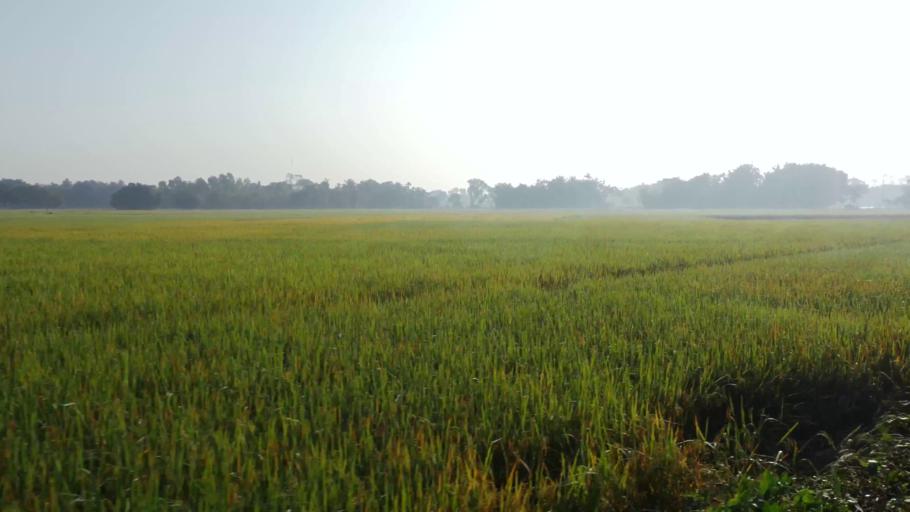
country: BD
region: Dhaka
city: Jamalpur
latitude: 24.9139
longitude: 89.9569
